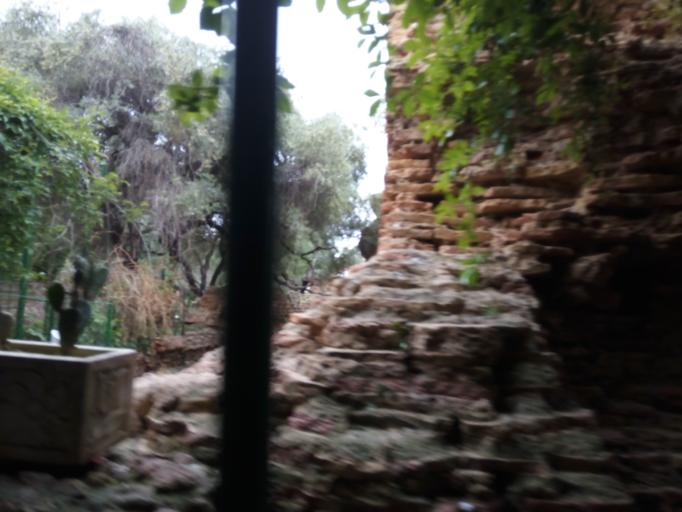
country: DZ
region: Tipaza
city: Tipasa
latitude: 36.5931
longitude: 2.4472
